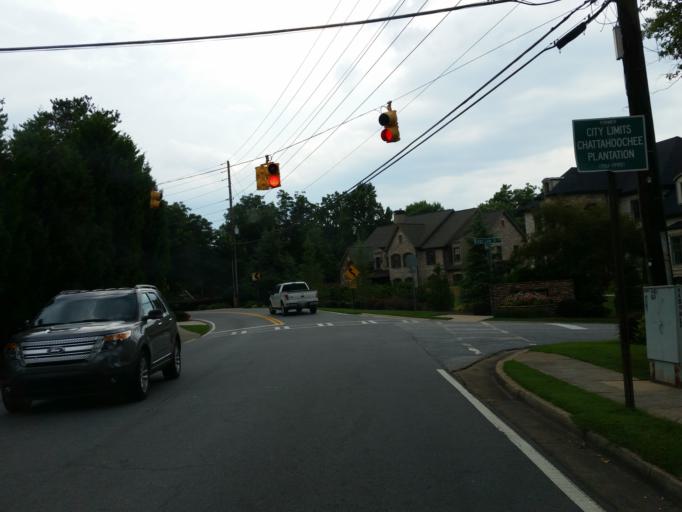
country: US
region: Georgia
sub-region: Fulton County
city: Sandy Springs
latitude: 33.9564
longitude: -84.4200
